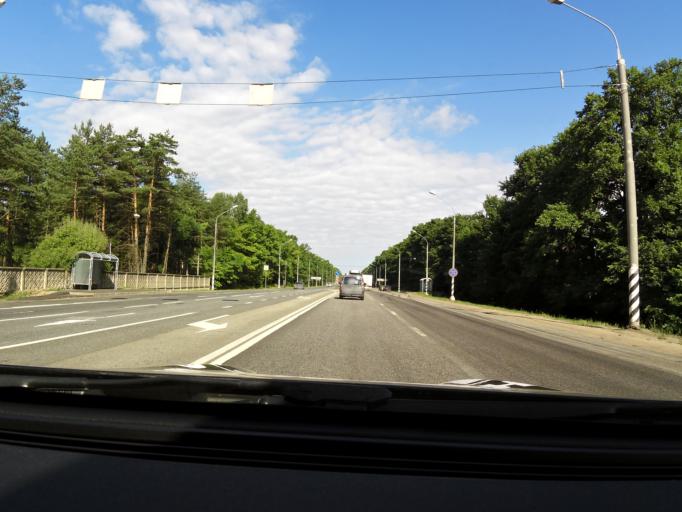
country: RU
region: Tverskaya
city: Radchenko
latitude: 56.6674
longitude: 36.4252
